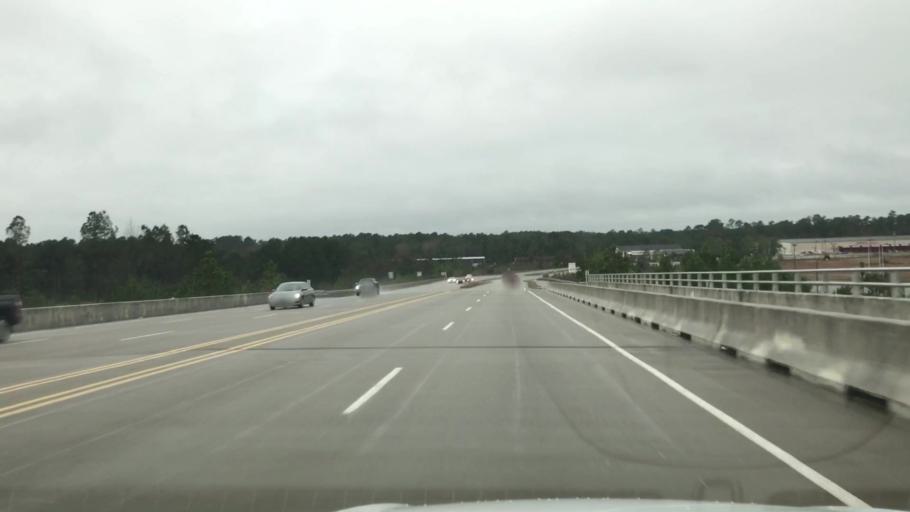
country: US
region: South Carolina
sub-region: Horry County
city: Forestbrook
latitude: 33.7067
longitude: -78.9367
